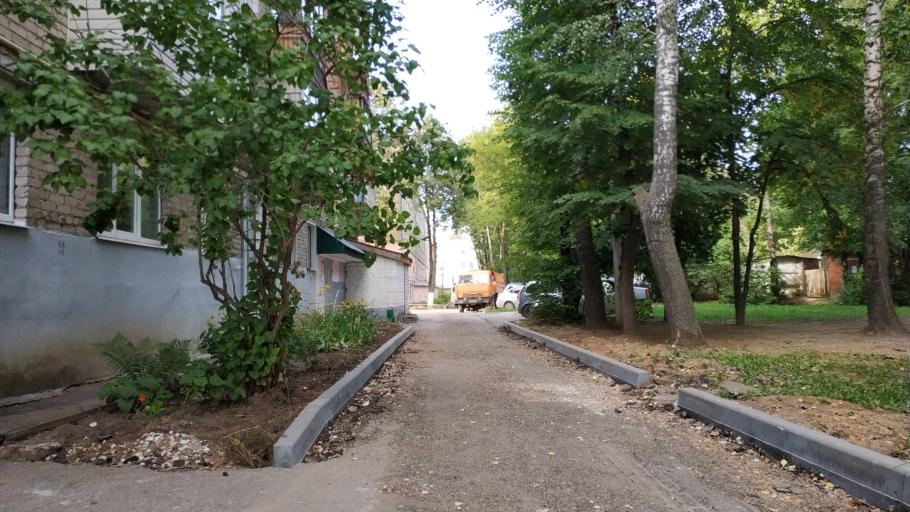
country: RU
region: Chuvashia
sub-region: Cheboksarskiy Rayon
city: Cheboksary
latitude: 56.1475
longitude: 47.2204
